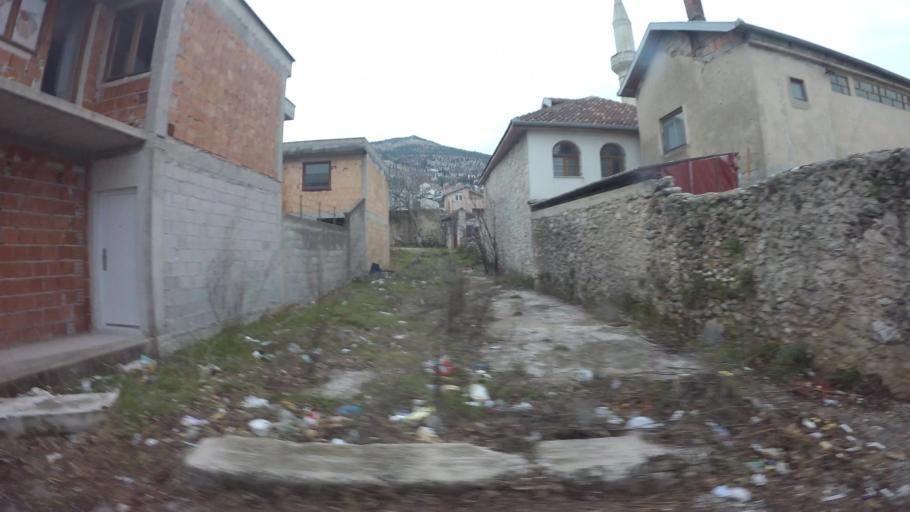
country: BA
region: Federation of Bosnia and Herzegovina
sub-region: Hercegovacko-Bosanski Kanton
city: Mostar
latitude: 43.3481
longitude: 17.8119
